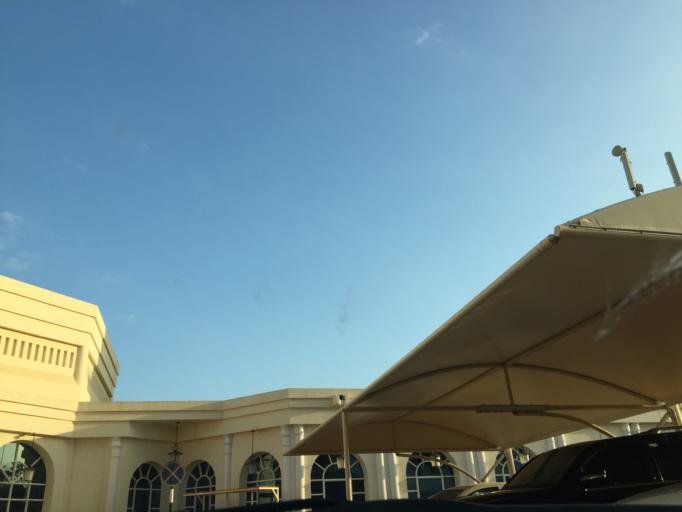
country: OM
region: Zufar
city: Salalah
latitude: 16.9815
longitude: 54.0149
